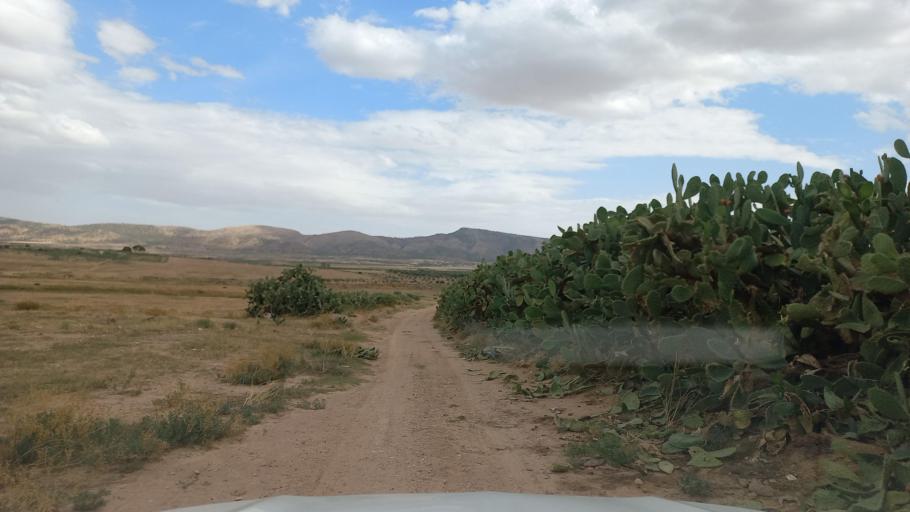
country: TN
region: Al Qasrayn
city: Sbiba
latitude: 35.3788
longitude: 9.1193
